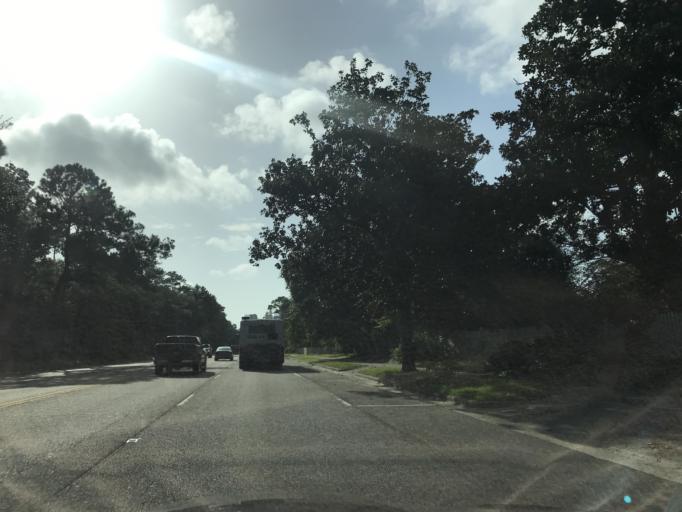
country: US
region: North Carolina
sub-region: New Hanover County
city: Wilmington
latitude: 34.2207
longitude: -77.9142
